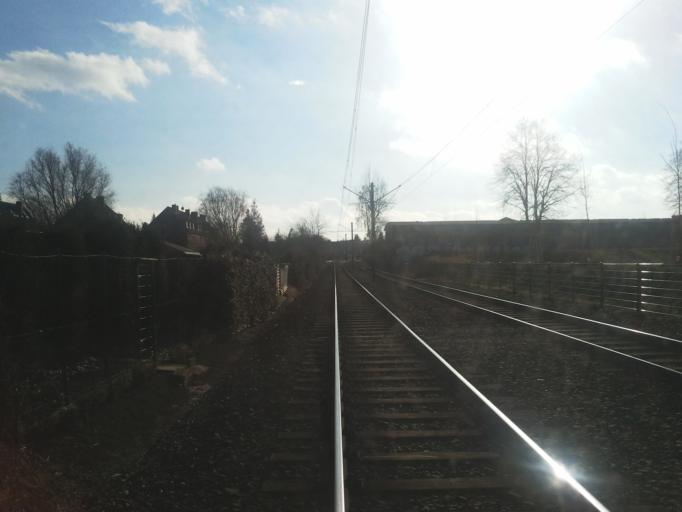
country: DE
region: Mecklenburg-Vorpommern
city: Kritzmow
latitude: 54.1087
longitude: 12.0800
